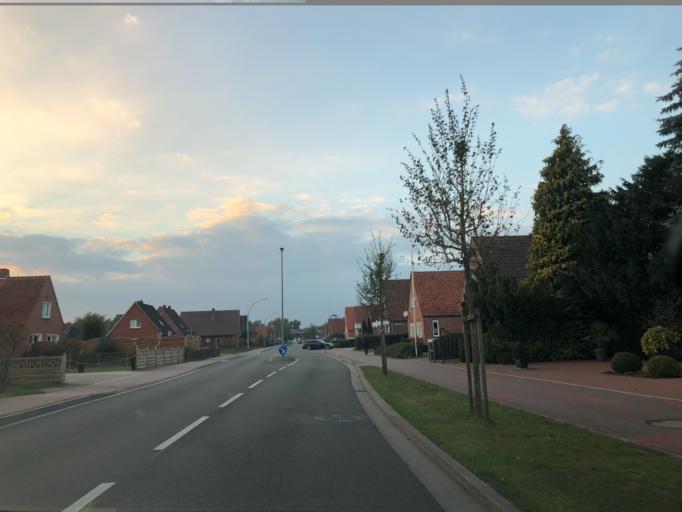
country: DE
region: Lower Saxony
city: Papenburg
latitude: 53.0676
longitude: 7.4305
